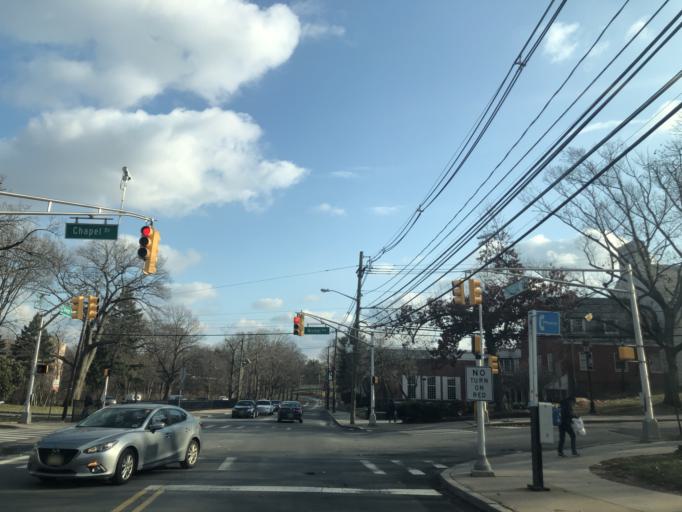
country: US
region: New Jersey
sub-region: Middlesex County
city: New Brunswick
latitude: 40.4855
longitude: -74.4372
